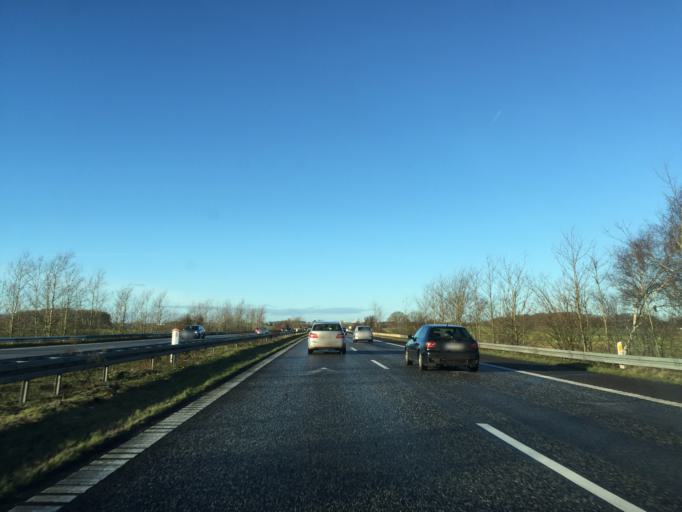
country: DK
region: South Denmark
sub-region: Middelfart Kommune
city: Ejby
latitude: 55.4332
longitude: 9.9848
